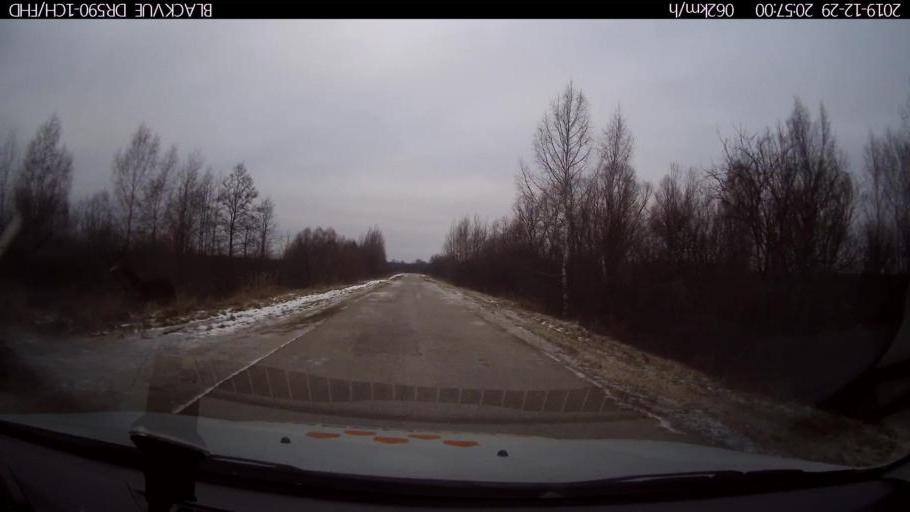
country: RU
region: Nizjnij Novgorod
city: Afonino
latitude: 56.1572
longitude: 43.9952
